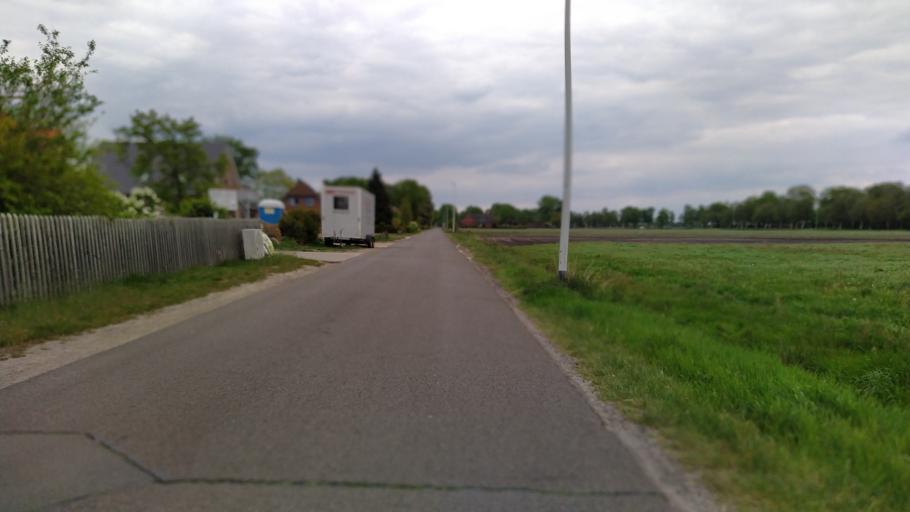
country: DE
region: Lower Saxony
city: Grasberg
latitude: 53.1832
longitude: 9.0088
